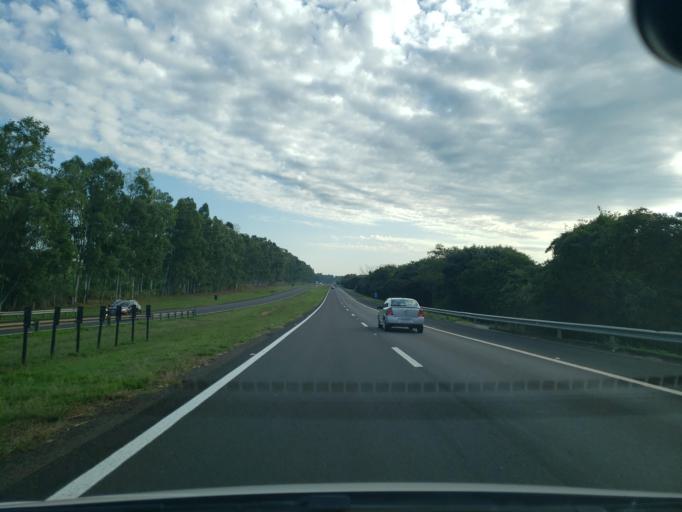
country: BR
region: Sao Paulo
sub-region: Guararapes
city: Guararapes
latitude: -21.2109
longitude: -50.6724
